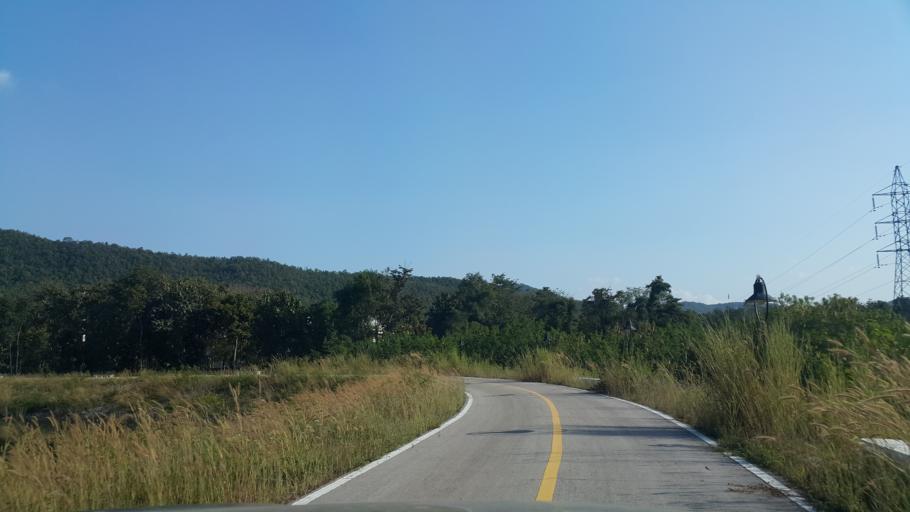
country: TH
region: Lamphun
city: Mae Tha
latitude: 18.5160
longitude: 99.1135
